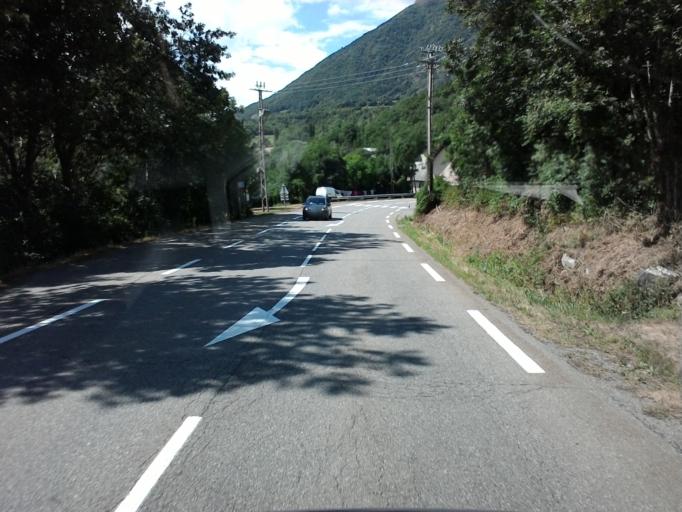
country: FR
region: Provence-Alpes-Cote d'Azur
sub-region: Departement des Hautes-Alpes
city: Saint-Bonnet-en-Champsaur
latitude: 44.7912
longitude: 5.9802
